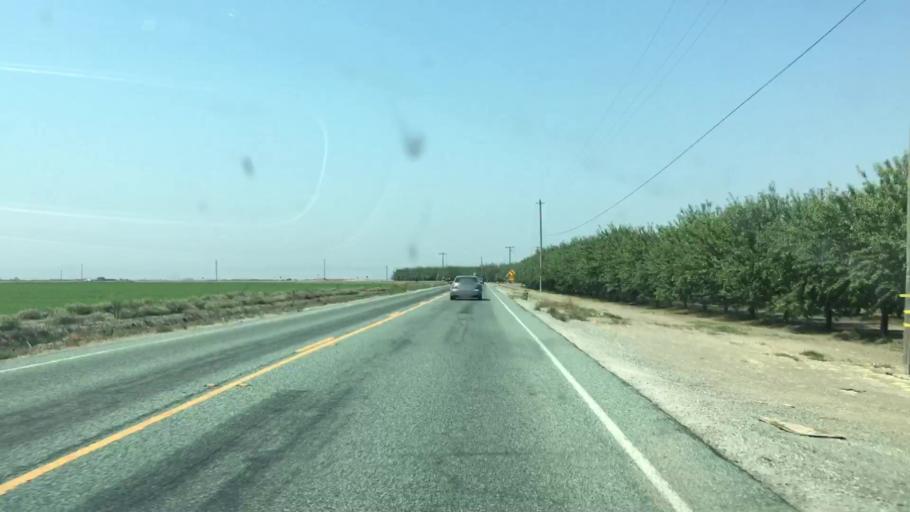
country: US
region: California
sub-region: San Joaquin County
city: Country Club
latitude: 37.8771
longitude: -121.3960
